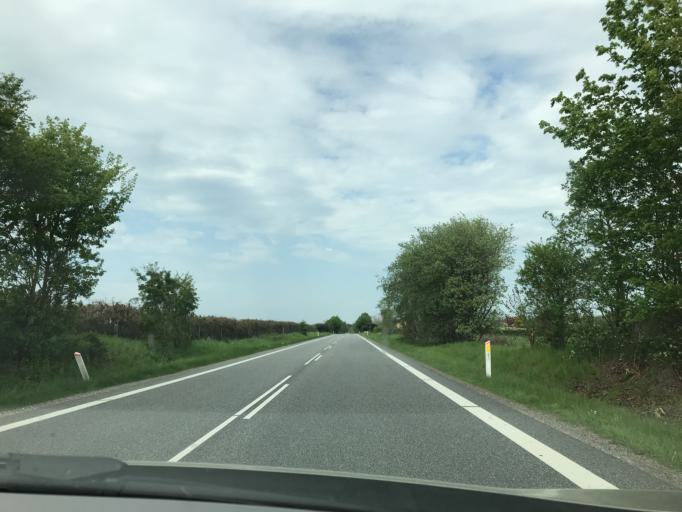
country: DK
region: South Denmark
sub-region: Assens Kommune
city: Assens
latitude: 55.3149
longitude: 9.9401
